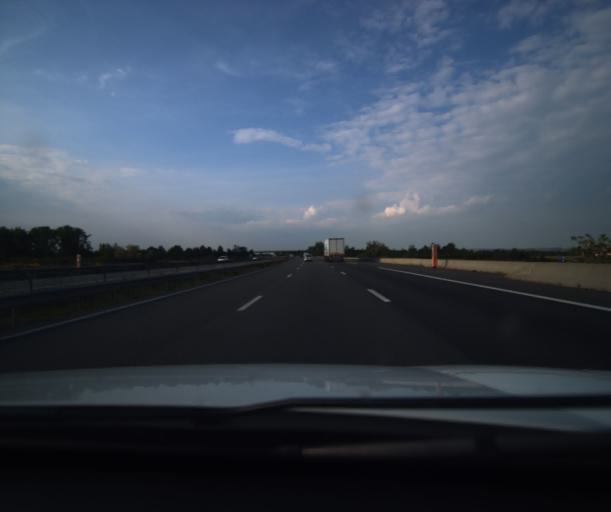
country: FR
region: Midi-Pyrenees
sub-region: Departement du Tarn-et-Garonne
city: Campsas
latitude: 43.9088
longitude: 1.3187
